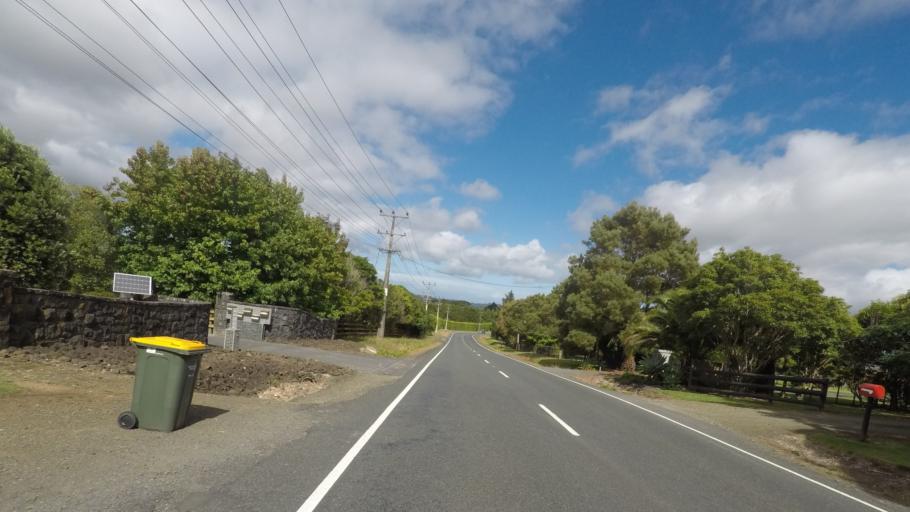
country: NZ
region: Auckland
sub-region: Auckland
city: Muriwai Beach
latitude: -36.7634
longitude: 174.5621
